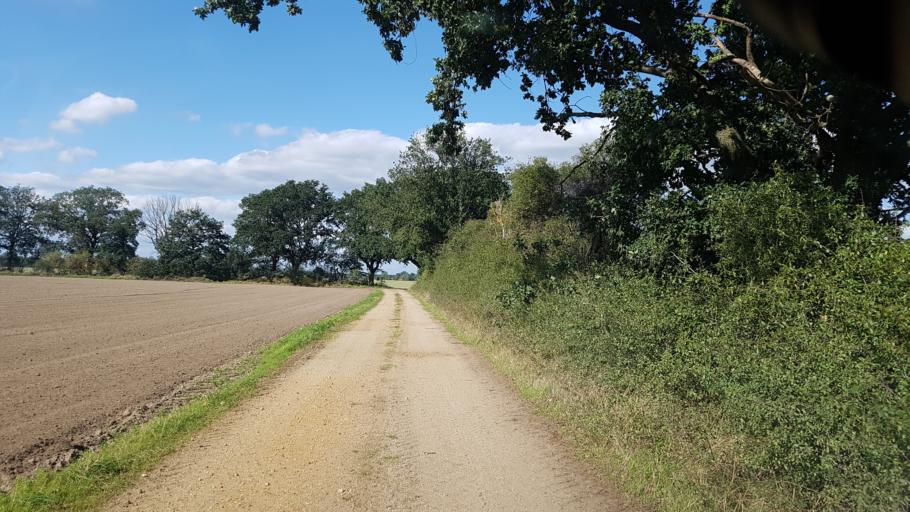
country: DE
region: Brandenburg
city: Sonnewalde
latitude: 51.6874
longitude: 13.6635
